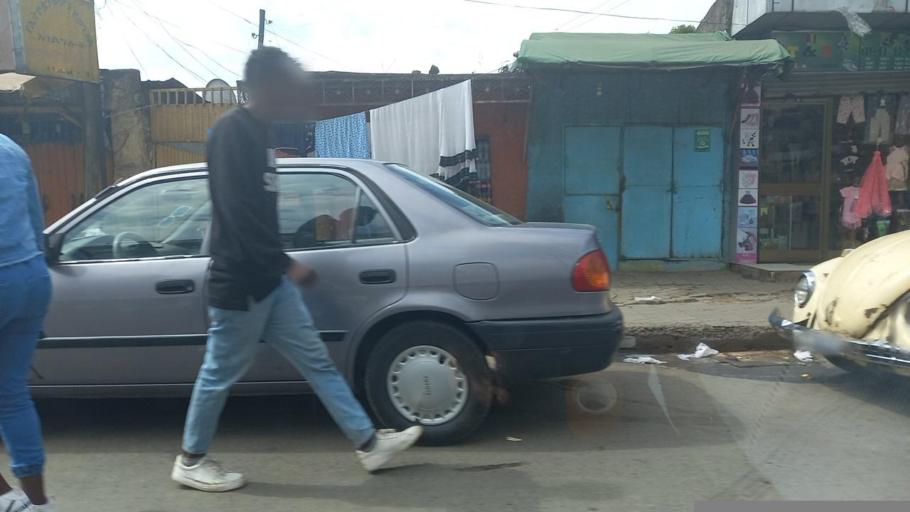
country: ET
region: Adis Abeba
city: Addis Ababa
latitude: 9.0413
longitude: 38.7502
